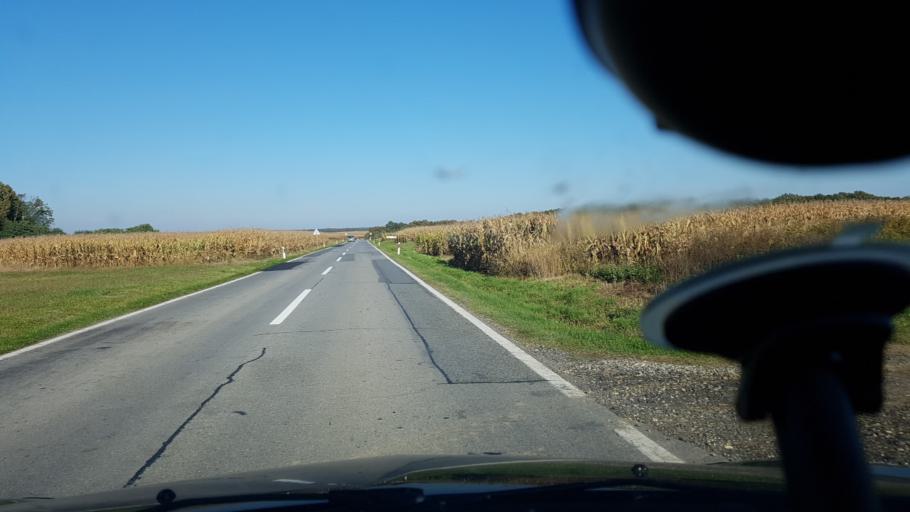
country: HR
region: Bjelovarsko-Bilogorska
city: Gudovac
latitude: 45.8249
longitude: 16.7432
